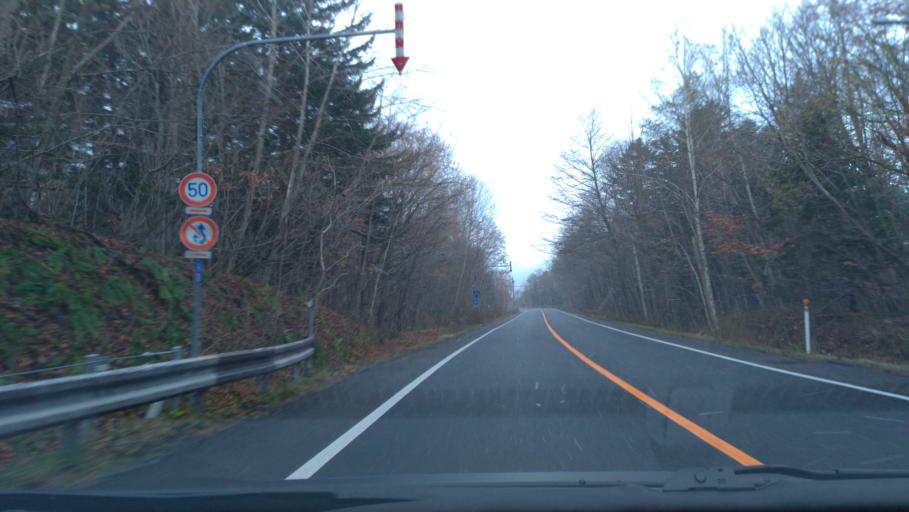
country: JP
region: Hokkaido
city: Shiraoi
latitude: 42.7413
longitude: 141.4057
